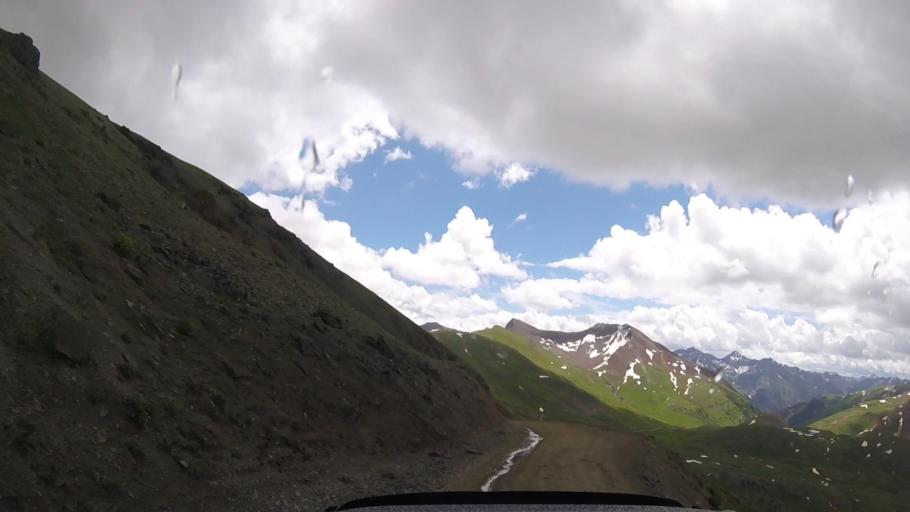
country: US
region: Colorado
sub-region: Ouray County
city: Ouray
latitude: 37.9672
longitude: -107.5872
